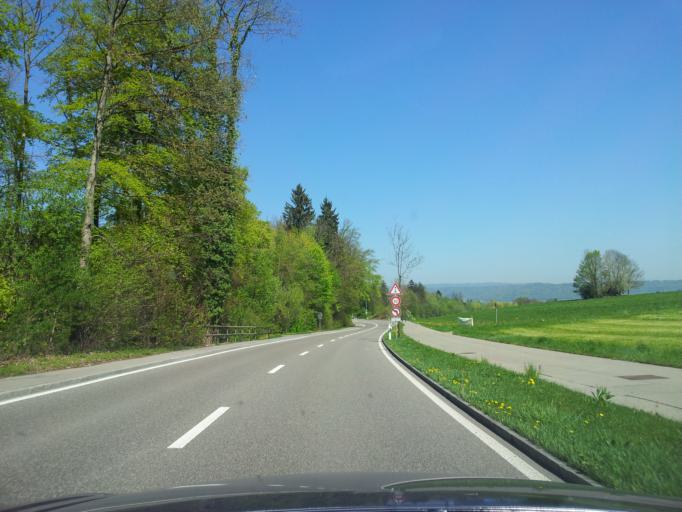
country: CH
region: Zurich
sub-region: Bezirk Dietikon
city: Urdorf / Oberurdorf
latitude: 47.3703
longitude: 8.4260
